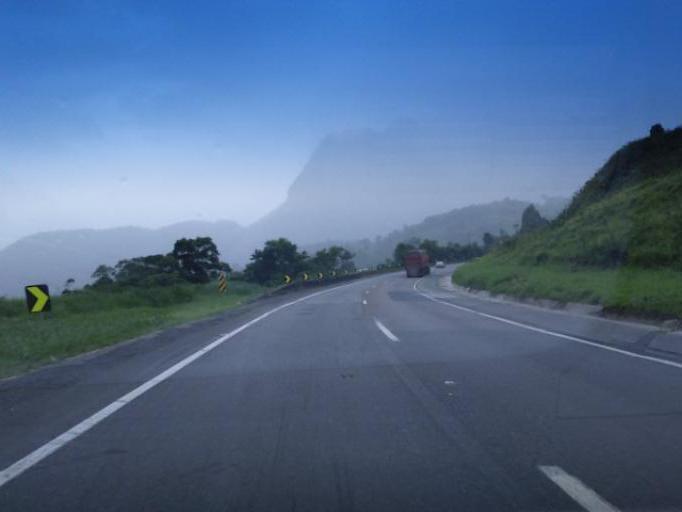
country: BR
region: Sao Paulo
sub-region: Cajati
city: Cajati
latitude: -24.8802
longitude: -48.2218
